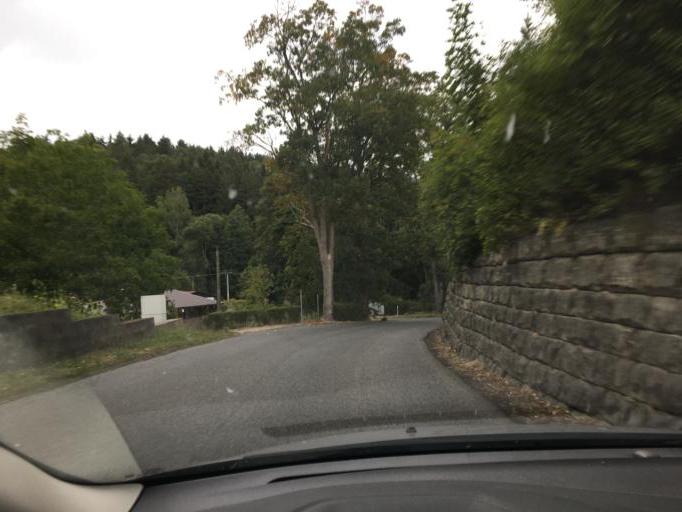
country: CZ
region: Ustecky
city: Ceska Kamenice
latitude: 50.8053
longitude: 14.3607
